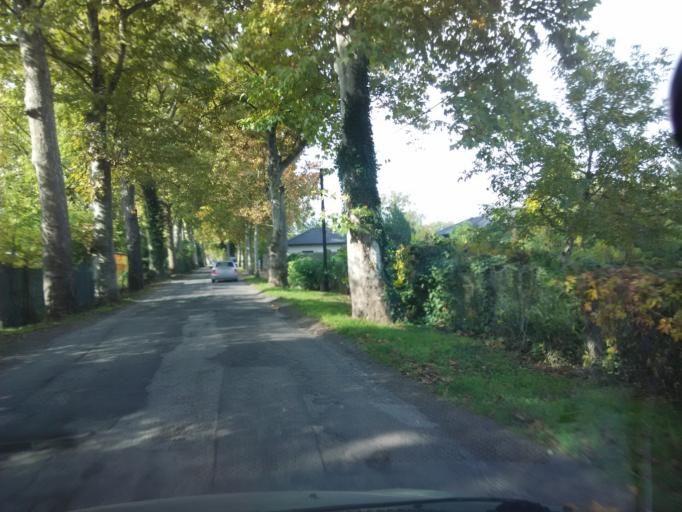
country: SK
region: Nitriansky
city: Komarno
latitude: 47.7554
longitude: 18.1123
